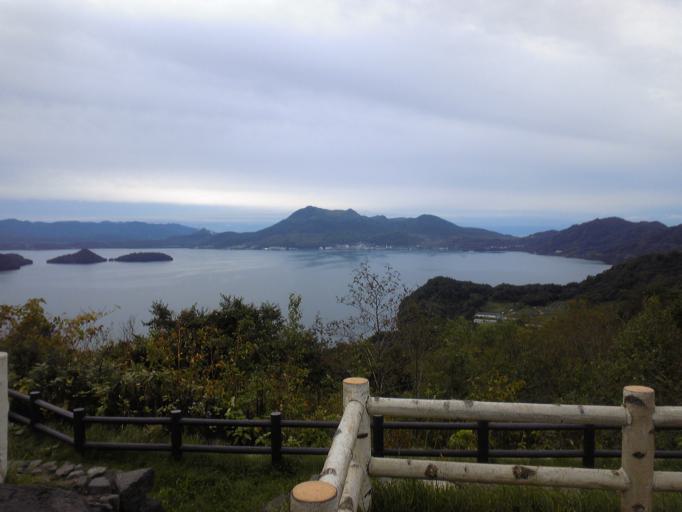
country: JP
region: Hokkaido
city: Date
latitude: 42.6258
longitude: 140.7997
